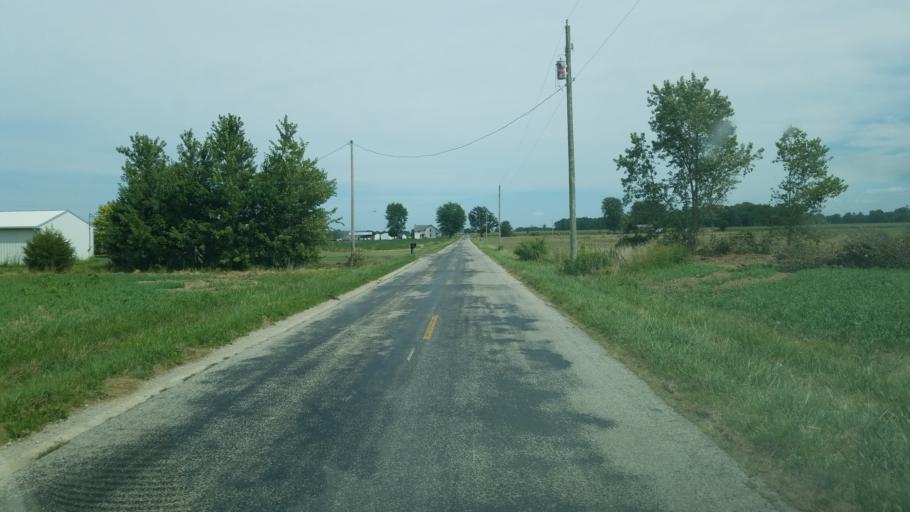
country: US
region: Ohio
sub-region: Union County
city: Richwood
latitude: 40.6074
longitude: -83.3198
